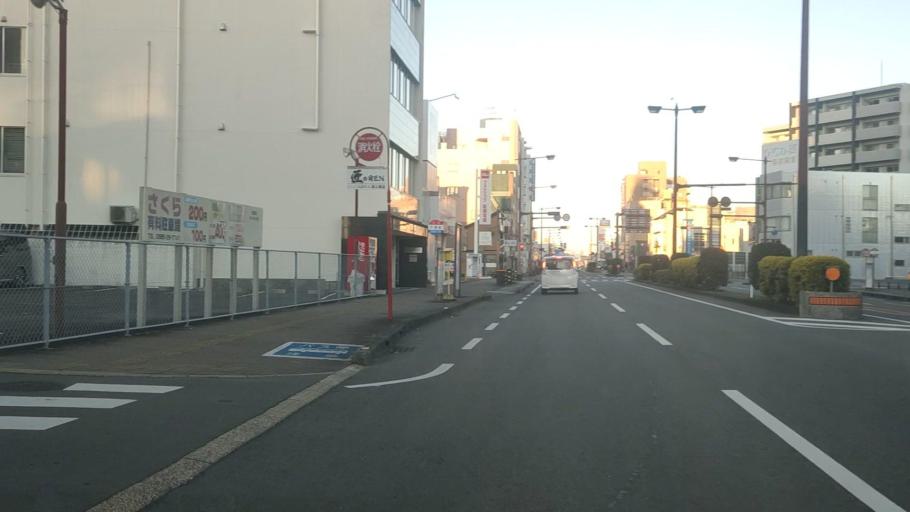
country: JP
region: Miyazaki
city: Miyazaki-shi
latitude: 31.9171
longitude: 131.4205
